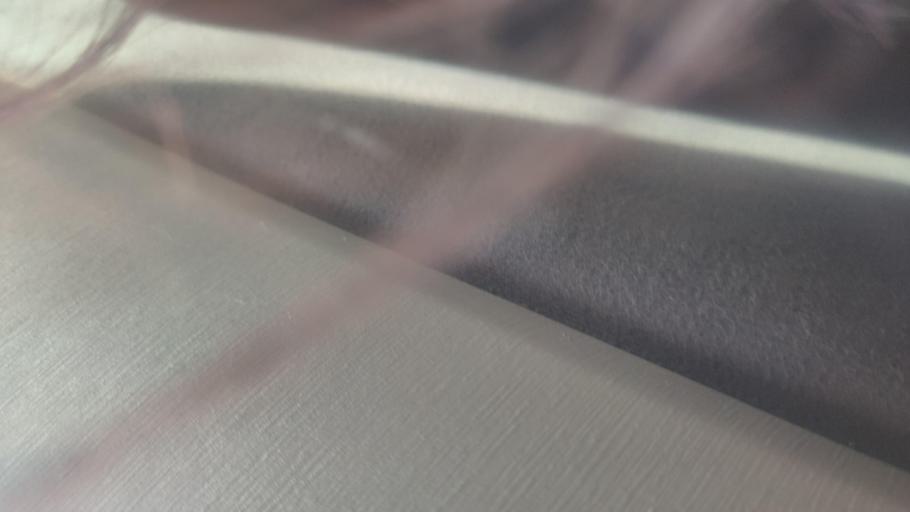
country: MN
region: Orhon
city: Erdenet
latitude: 49.0263
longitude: 104.0378
